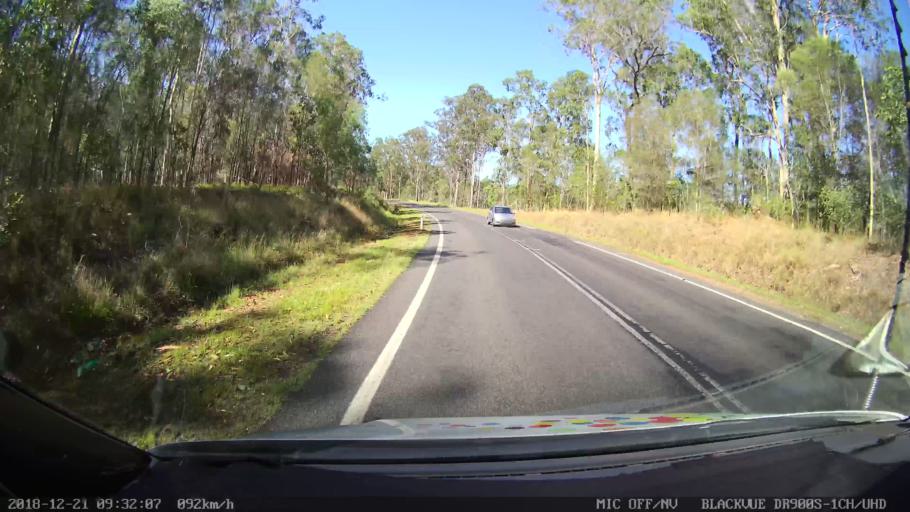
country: AU
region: New South Wales
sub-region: Clarence Valley
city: Maclean
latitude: -29.4666
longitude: 152.9805
